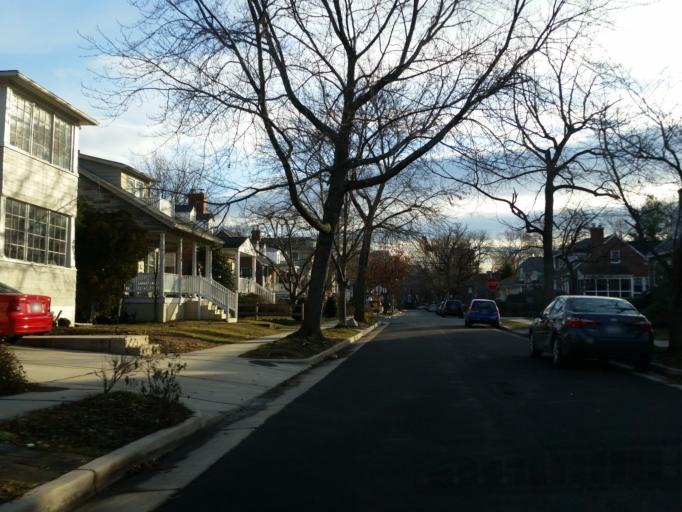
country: US
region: Virginia
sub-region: City of Alexandria
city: Alexandria
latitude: 38.8116
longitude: -77.0591
